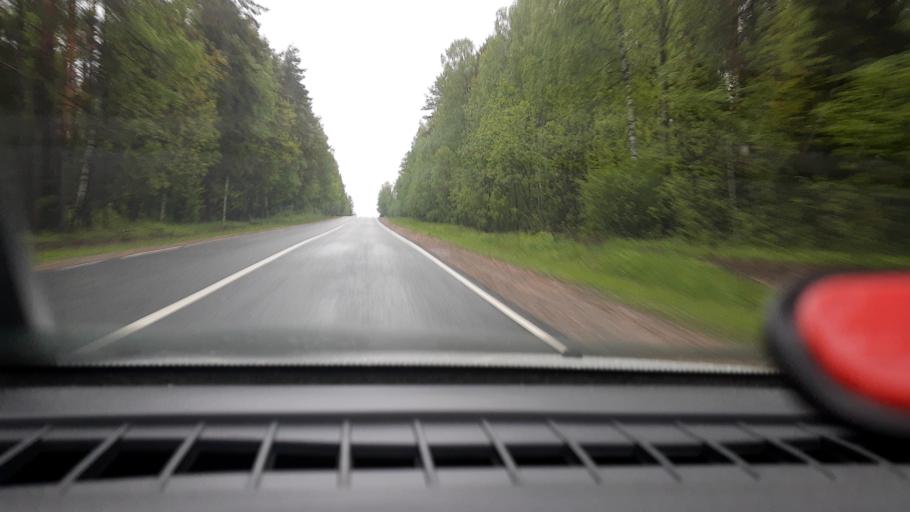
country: RU
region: Nizjnij Novgorod
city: Krasnyye Baki
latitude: 56.9963
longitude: 45.1139
